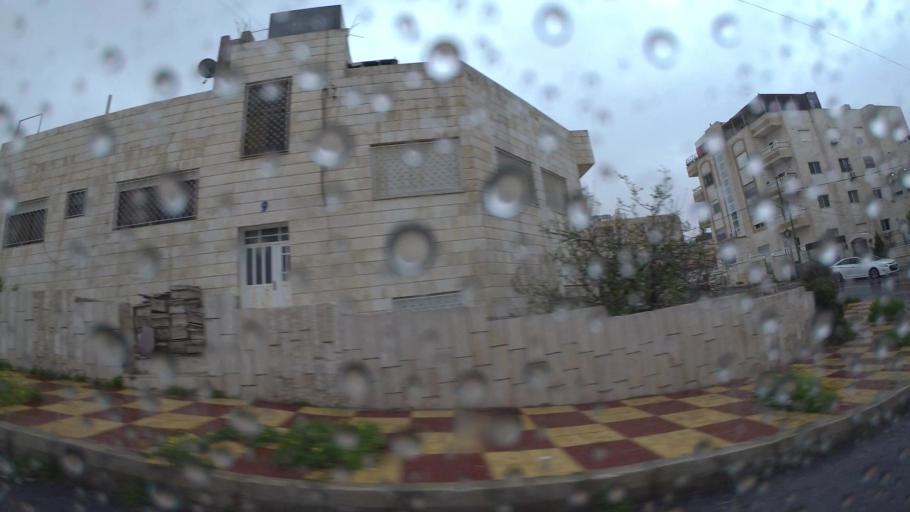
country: JO
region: Amman
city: Amman
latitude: 32.0034
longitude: 35.9577
